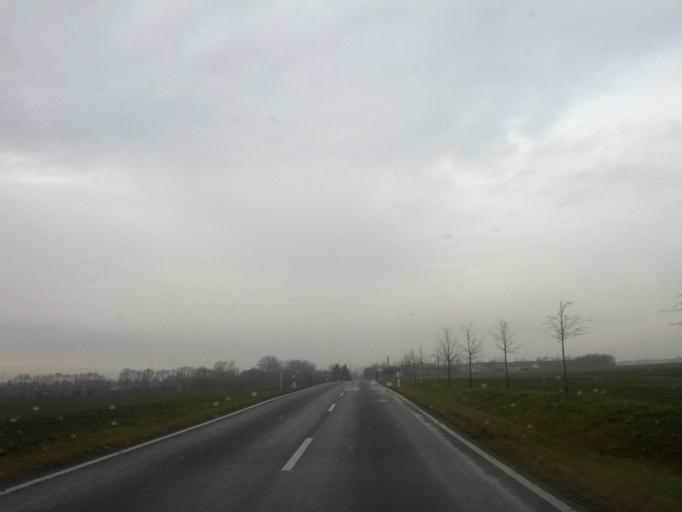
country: DE
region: Thuringia
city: Nottleben
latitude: 50.9683
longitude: 10.8638
